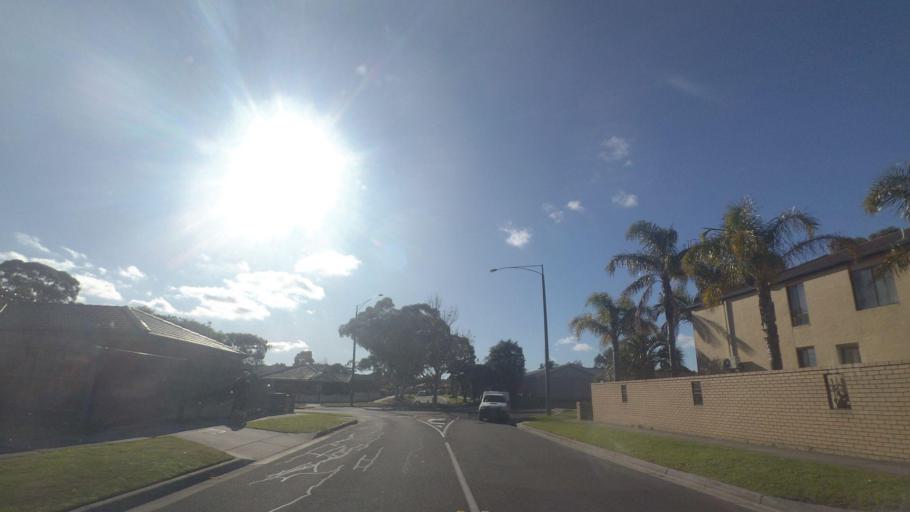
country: AU
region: Victoria
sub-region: Knox
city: Rowville
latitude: -37.9319
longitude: 145.2492
